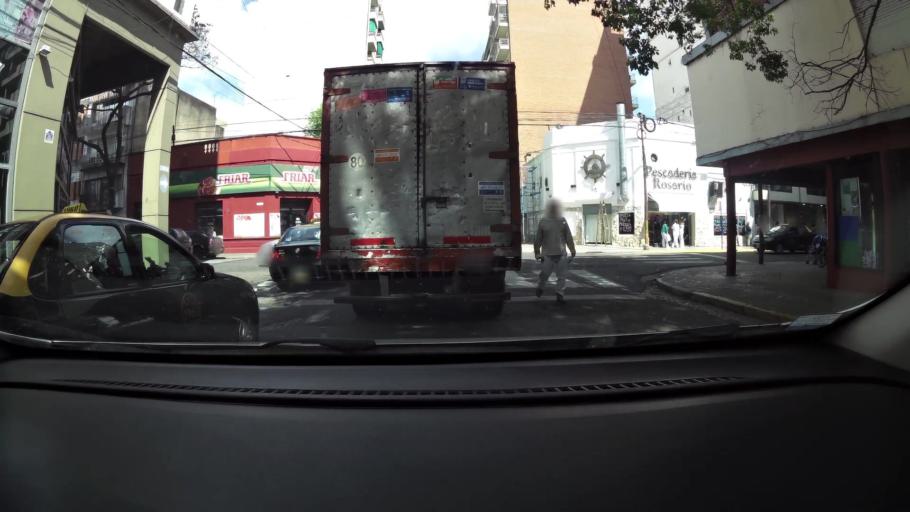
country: AR
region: Santa Fe
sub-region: Departamento de Rosario
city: Rosario
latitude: -32.9540
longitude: -60.6458
